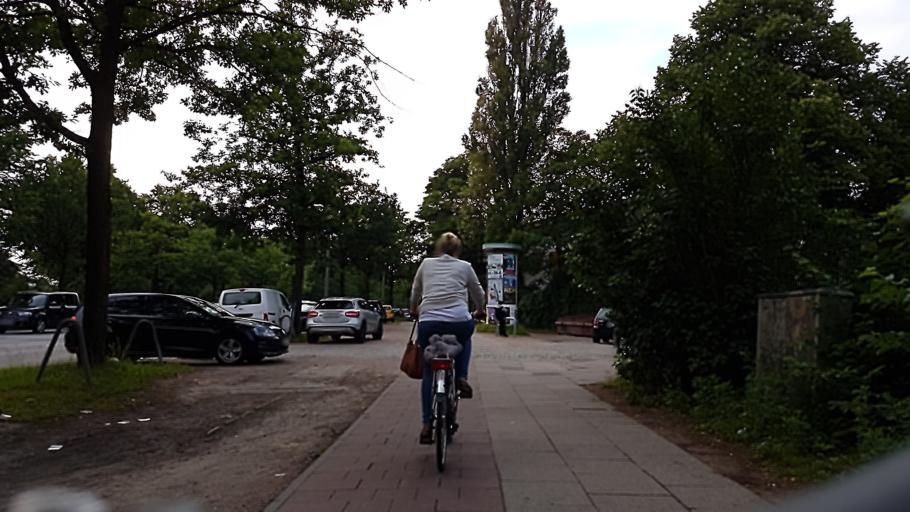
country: DE
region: Hamburg
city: Winterhude
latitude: 53.5905
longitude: 10.0116
